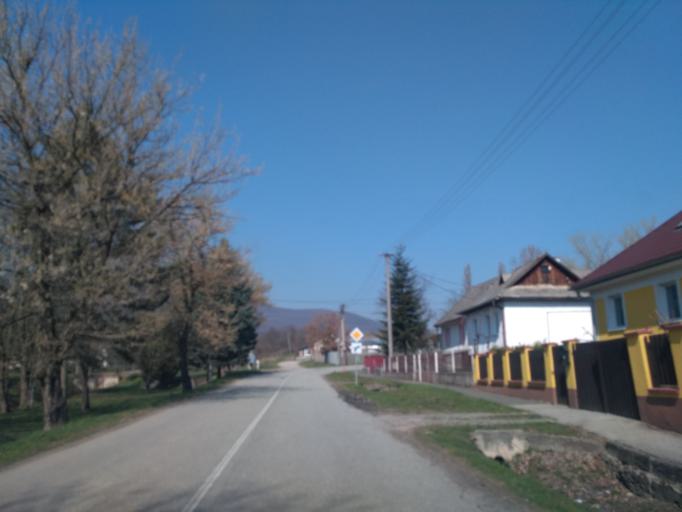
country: SK
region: Kosicky
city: Secovce
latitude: 48.7658
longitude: 21.6580
